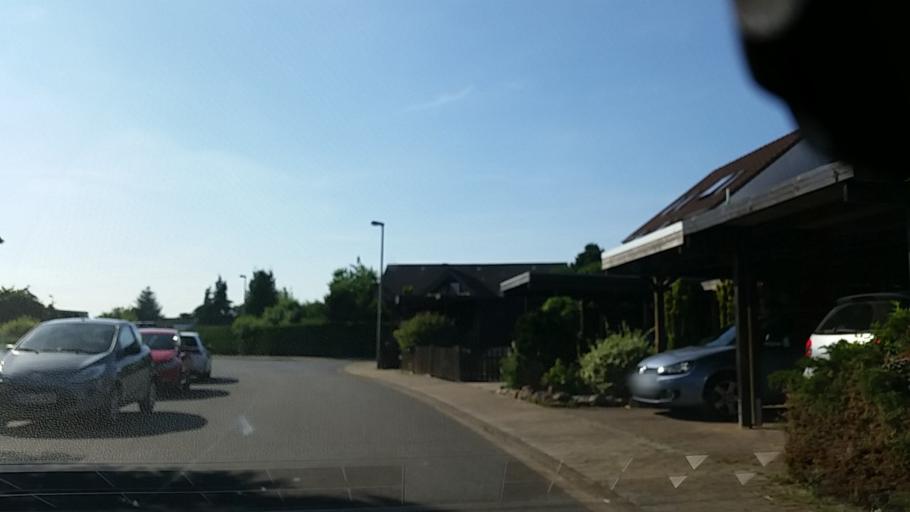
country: DE
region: Lower Saxony
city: Wolfsburg
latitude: 52.4002
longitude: 10.7305
